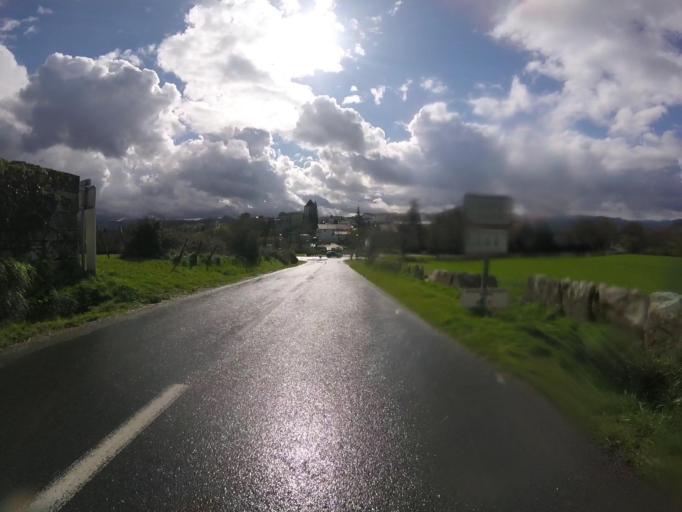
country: FR
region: Aquitaine
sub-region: Departement des Pyrenees-Atlantiques
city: Sare
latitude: 43.3152
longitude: -1.5836
